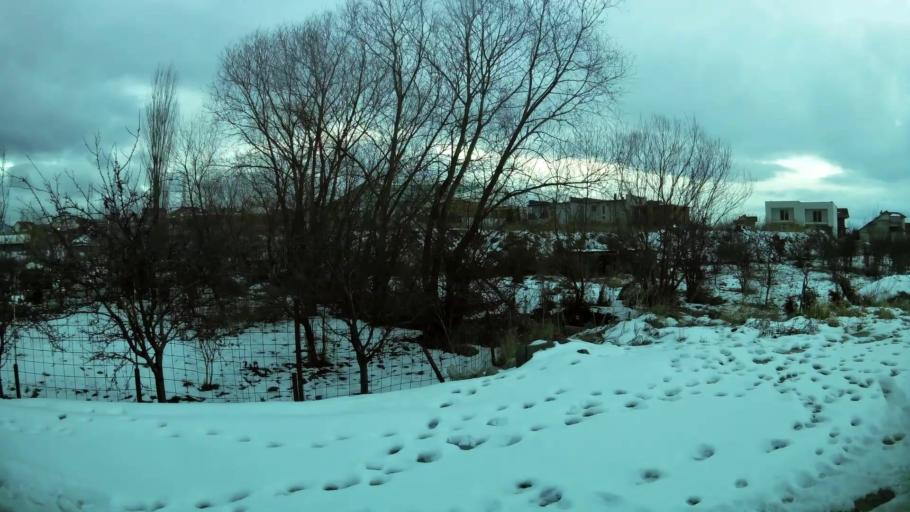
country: XK
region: Pristina
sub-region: Komuna e Prishtines
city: Pristina
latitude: 42.6179
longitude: 21.1671
